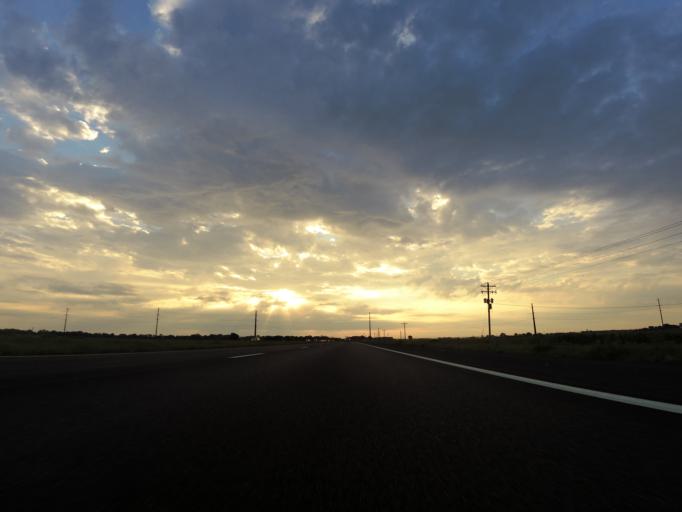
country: US
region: Kansas
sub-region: Sedgwick County
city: Colwich
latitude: 37.8248
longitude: -97.5279
